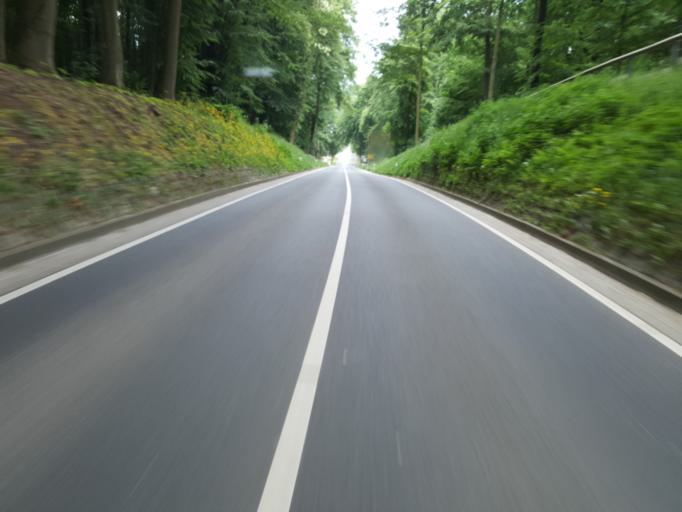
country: DE
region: Lower Saxony
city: Rehburg-Loccum
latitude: 52.4430
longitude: 9.2161
